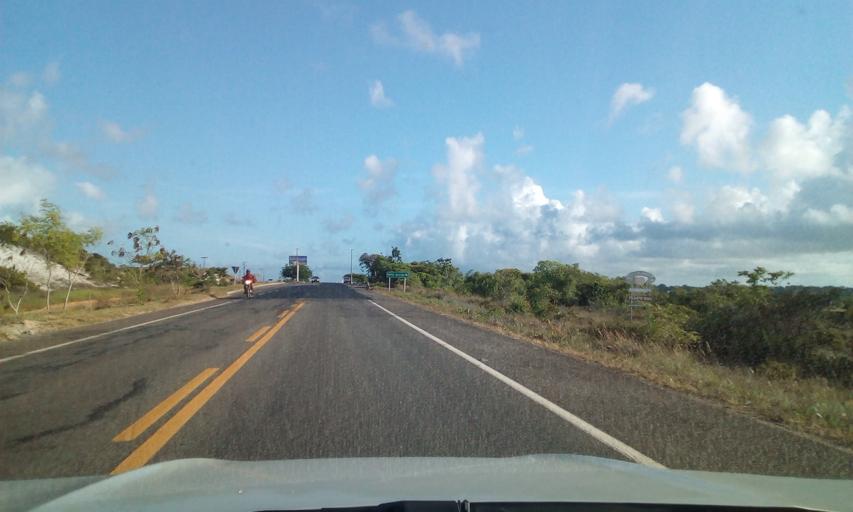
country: BR
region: Bahia
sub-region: Mata De Sao Joao
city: Mata de Sao Joao
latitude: -12.3714
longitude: -37.9097
